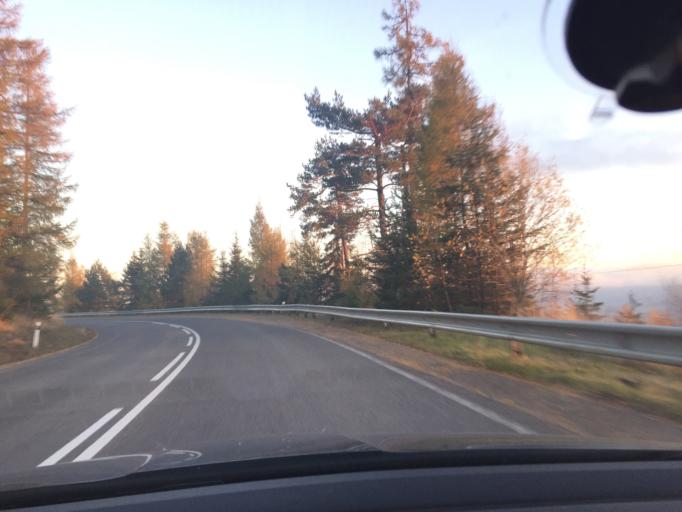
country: SK
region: Presovsky
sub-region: Okres Poprad
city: Strba
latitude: 49.1176
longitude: 20.1376
